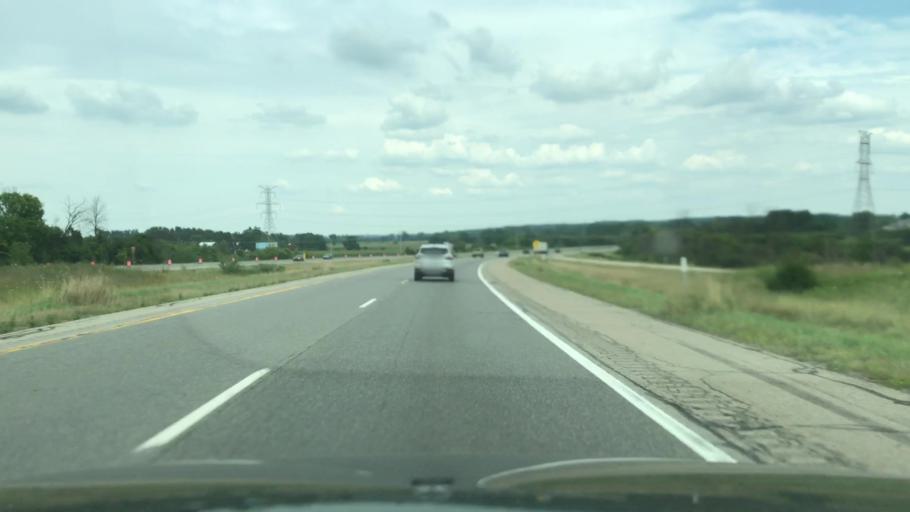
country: US
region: Michigan
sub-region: Ottawa County
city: Zeeland
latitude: 42.8140
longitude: -85.9786
